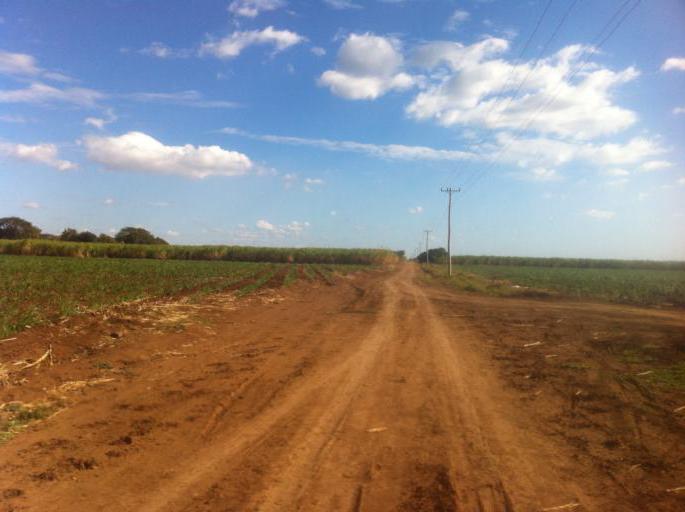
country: NI
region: Managua
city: Carlos Fonseca Amador
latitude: 11.9100
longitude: -86.5922
